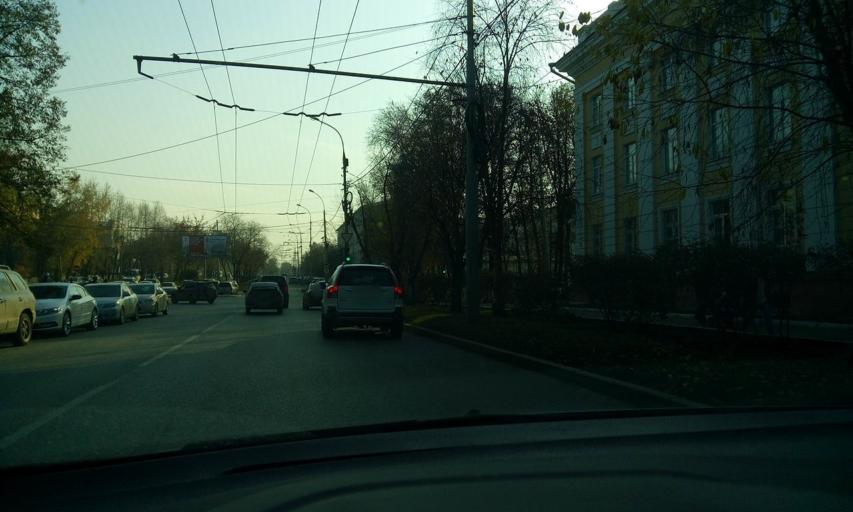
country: RU
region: Sverdlovsk
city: Yekaterinburg
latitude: 56.8467
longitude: 60.6492
